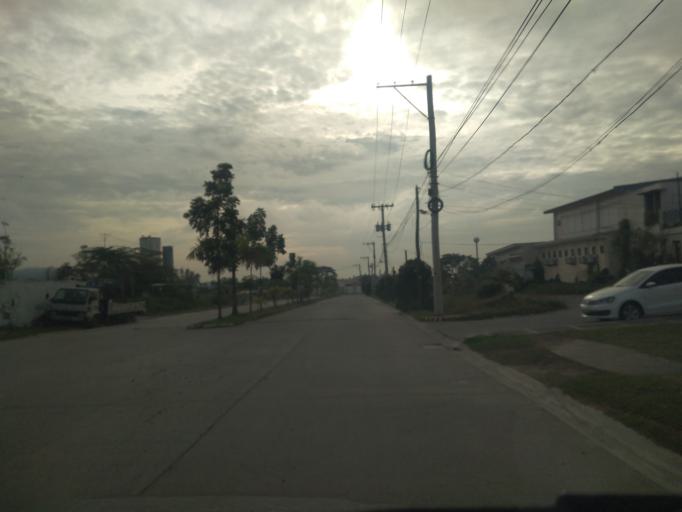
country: PH
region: Central Luzon
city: Santol
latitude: 15.1665
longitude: 120.5385
